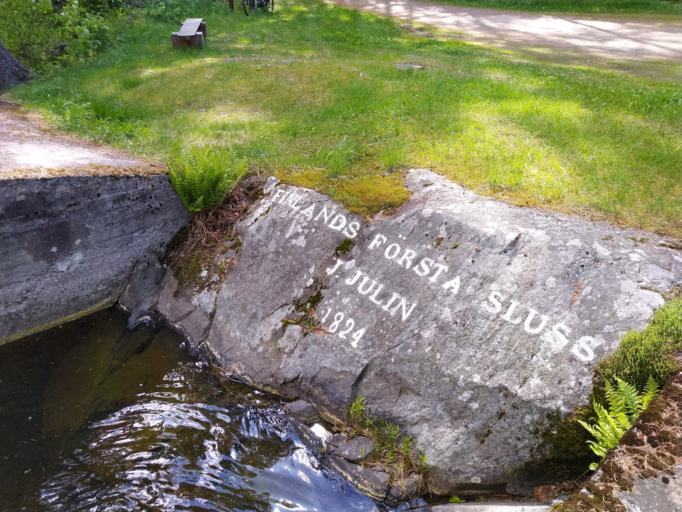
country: FI
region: Uusimaa
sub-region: Raaseporin
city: Pohja
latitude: 60.1762
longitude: 23.5938
